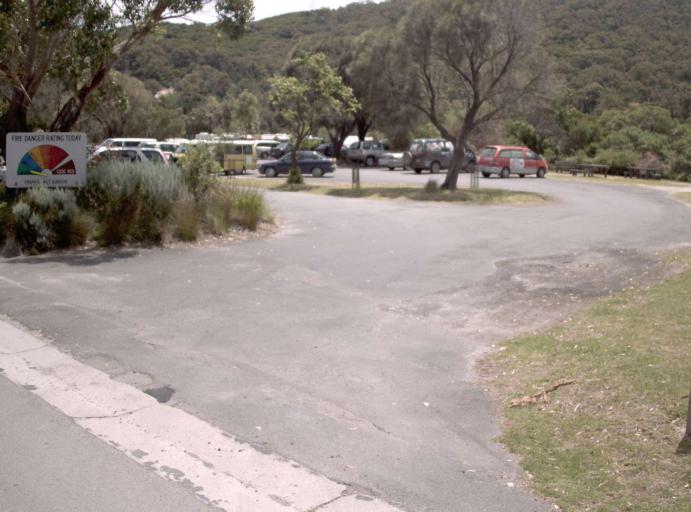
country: AU
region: Victoria
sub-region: Latrobe
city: Morwell
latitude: -39.0306
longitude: 146.3226
